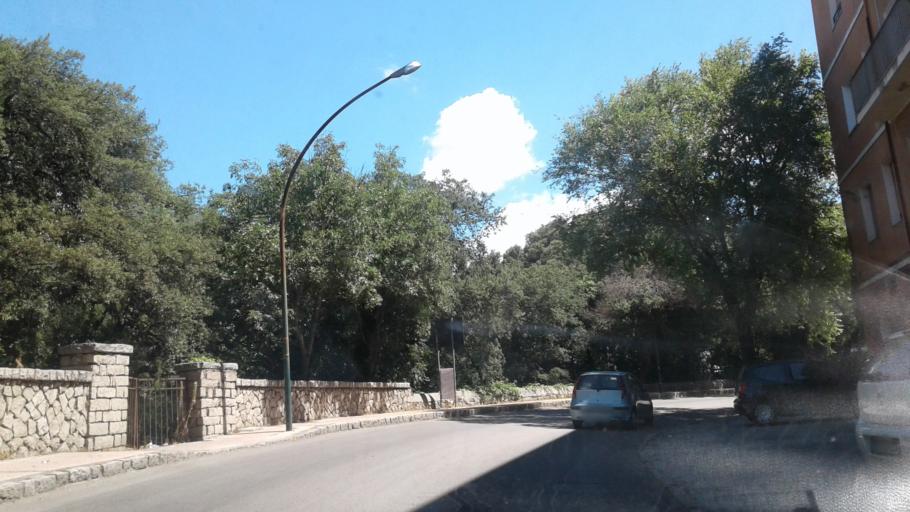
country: IT
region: Sardinia
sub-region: Provincia di Olbia-Tempio
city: Tempio Pausania
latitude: 40.9061
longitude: 9.1012
